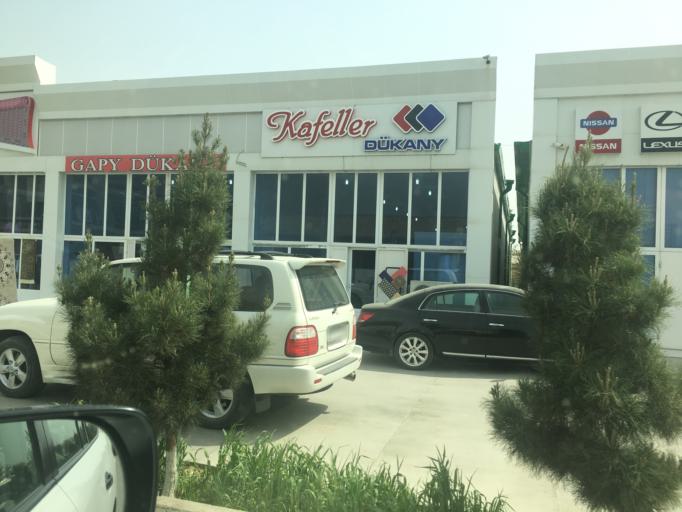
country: TM
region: Mary
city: Mary
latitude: 37.6029
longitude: 61.8374
